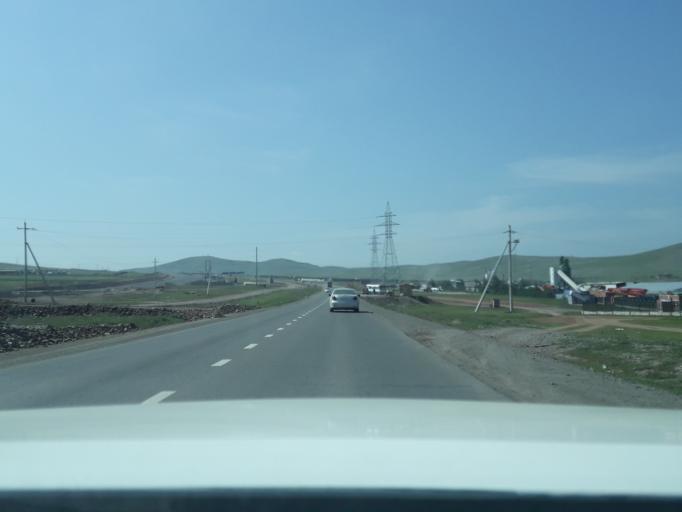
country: MN
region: Ulaanbaatar
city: Ulaanbaatar
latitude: 47.8207
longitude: 106.7611
